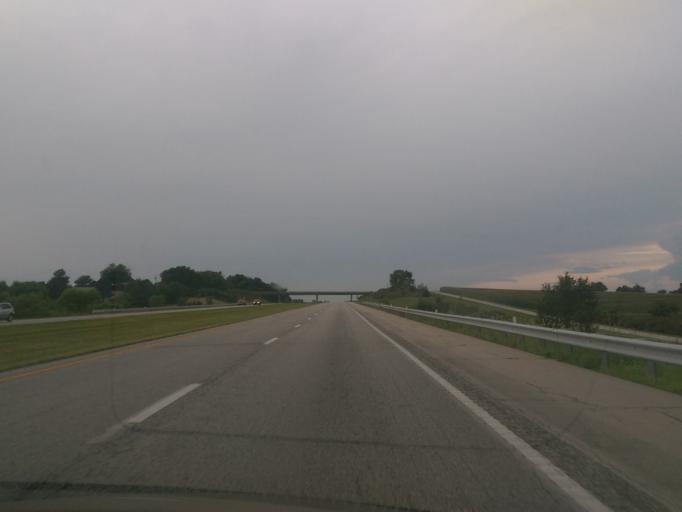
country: US
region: Missouri
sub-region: Holt County
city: Oregon
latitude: 40.0124
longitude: -95.0811
